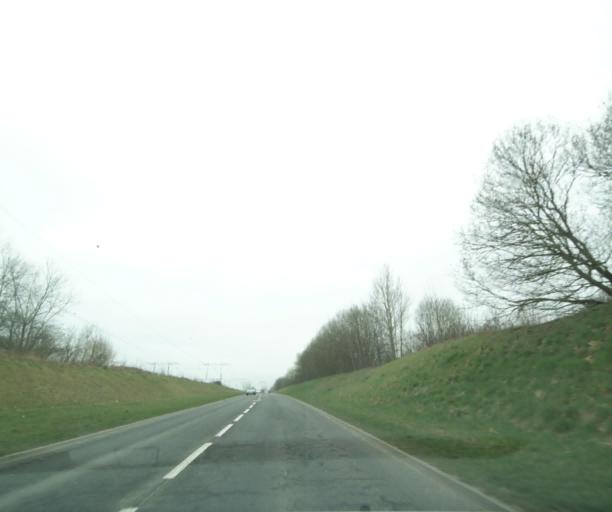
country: FR
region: Ile-de-France
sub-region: Departement du Val-d'Oise
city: Courdimanche
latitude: 49.0524
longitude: 2.0011
